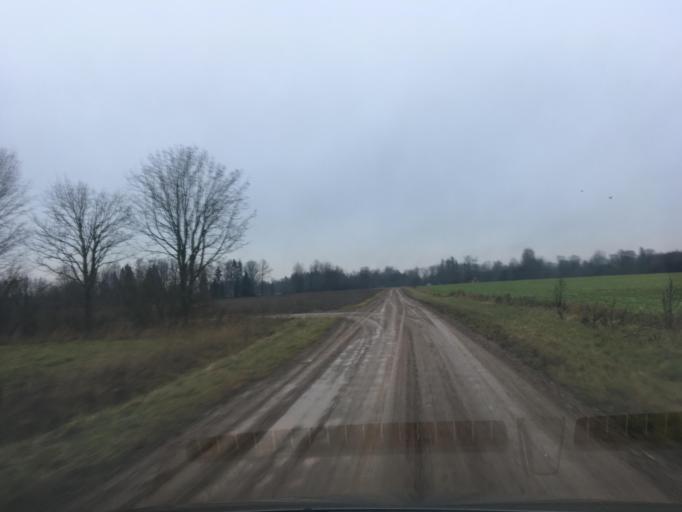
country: EE
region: Tartu
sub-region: Tartu linn
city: Tartu
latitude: 58.3900
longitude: 26.9281
